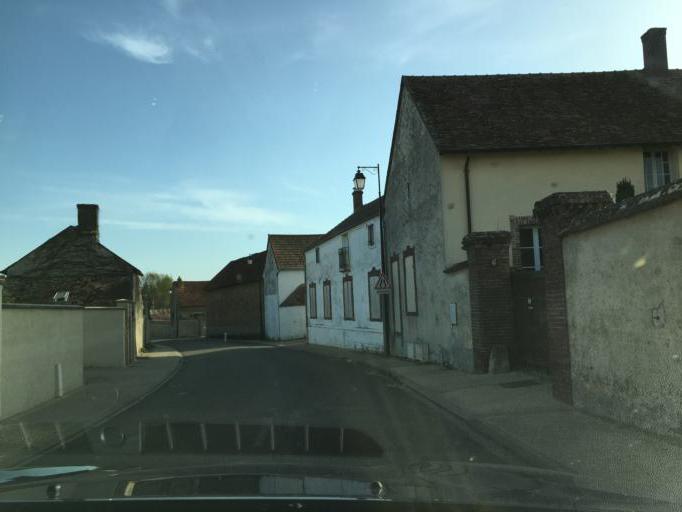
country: FR
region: Ile-de-France
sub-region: Departement des Yvelines
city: Conde-sur-Vesgre
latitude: 48.7231
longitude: 1.6537
